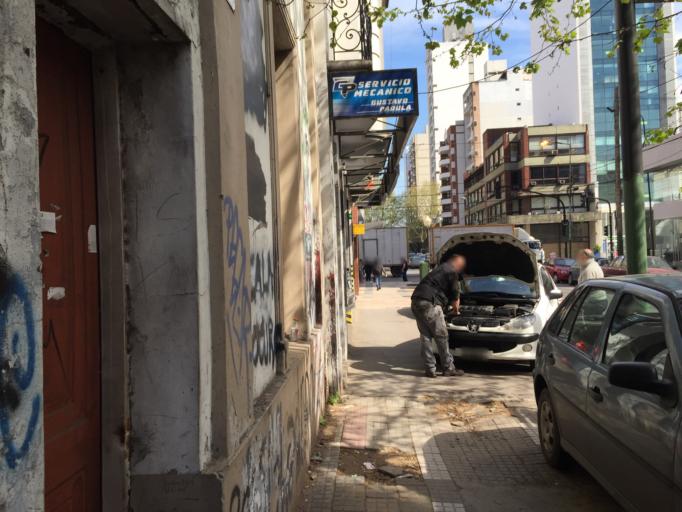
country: AR
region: Buenos Aires
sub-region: Partido de Lomas de Zamora
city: Lomas de Zamora
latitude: -34.7628
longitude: -58.4025
